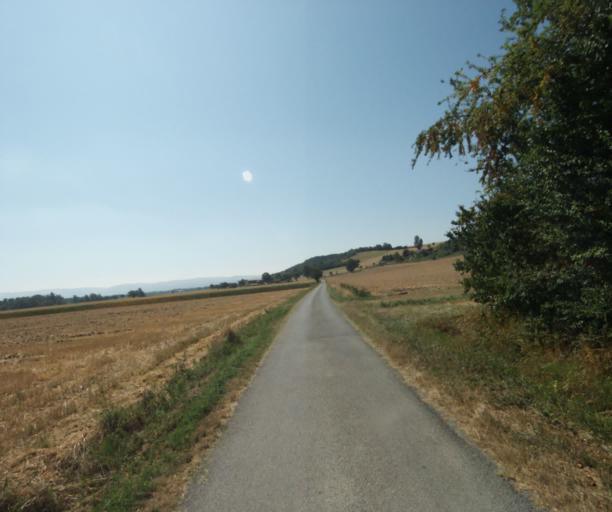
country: FR
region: Midi-Pyrenees
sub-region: Departement du Tarn
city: Puylaurens
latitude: 43.5240
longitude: 1.9417
